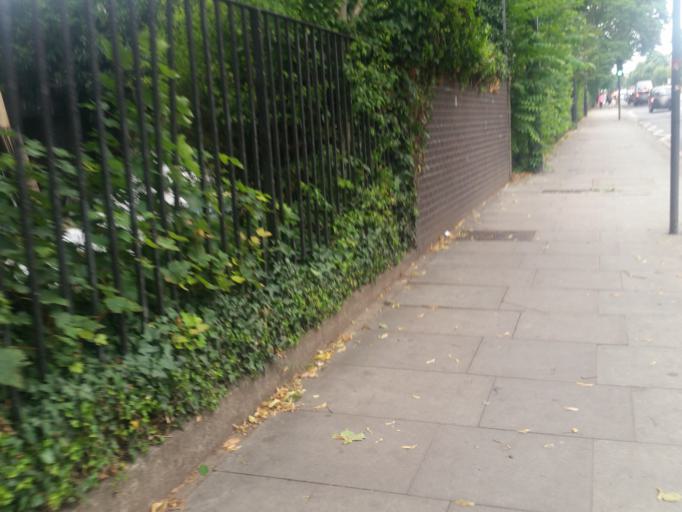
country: GB
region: England
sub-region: Greater London
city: Camden Town
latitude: 51.5447
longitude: -0.1350
